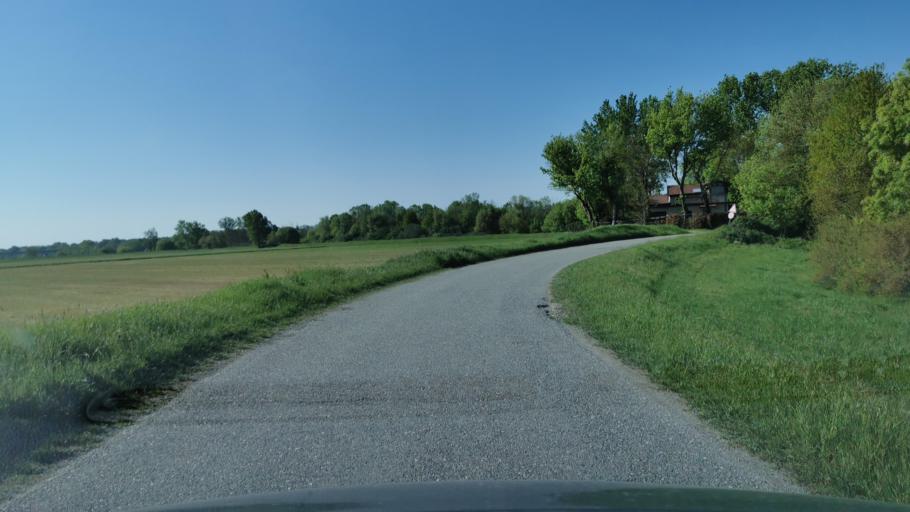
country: IT
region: Lombardy
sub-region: Provincia di Cremona
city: Bosco Ex Parmigiano
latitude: 45.1118
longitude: 10.0175
